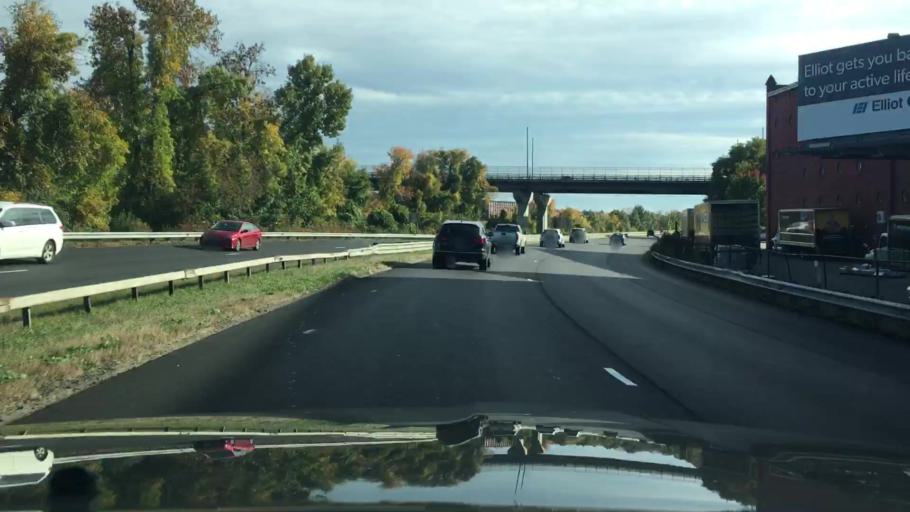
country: US
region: New Hampshire
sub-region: Hillsborough County
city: Manchester
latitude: 42.9959
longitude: -71.4709
